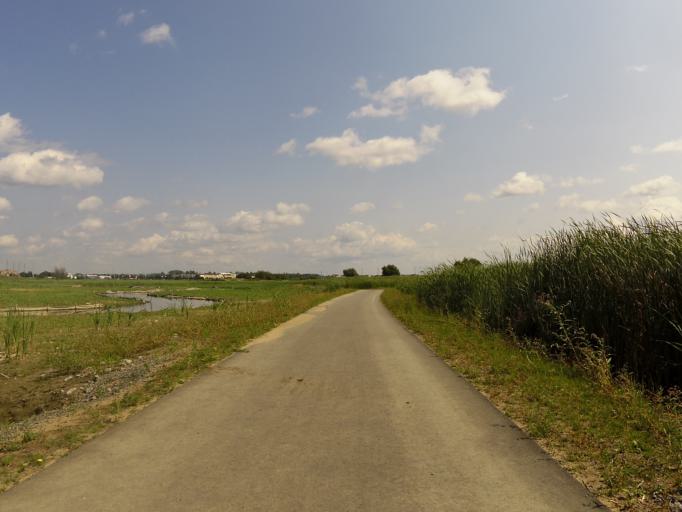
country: CA
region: Ontario
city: Bells Corners
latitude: 45.3088
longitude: -75.9315
